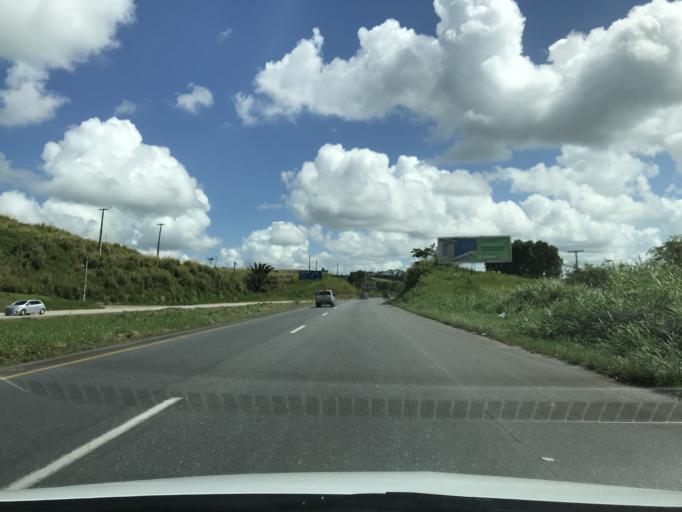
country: BR
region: Pernambuco
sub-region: Jaboatao Dos Guararapes
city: Jaboatao dos Guararapes
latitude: -8.0964
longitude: -35.0485
